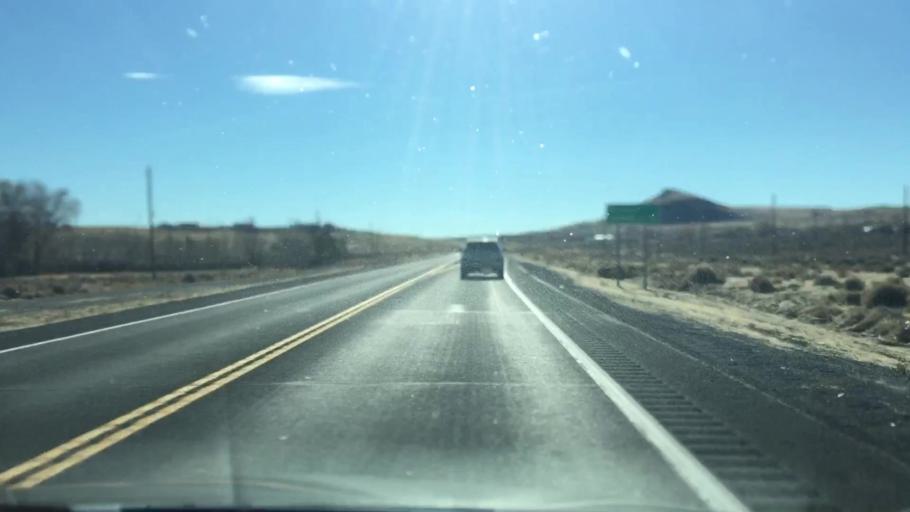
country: US
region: Nevada
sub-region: Lyon County
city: Silver Springs
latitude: 39.3490
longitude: -119.2392
